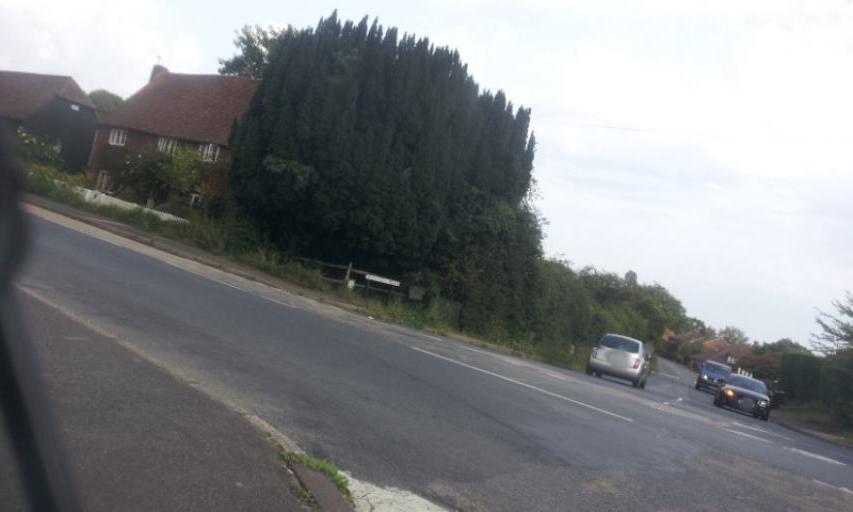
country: GB
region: England
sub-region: Kent
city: Paddock Wood
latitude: 51.1539
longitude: 0.3734
